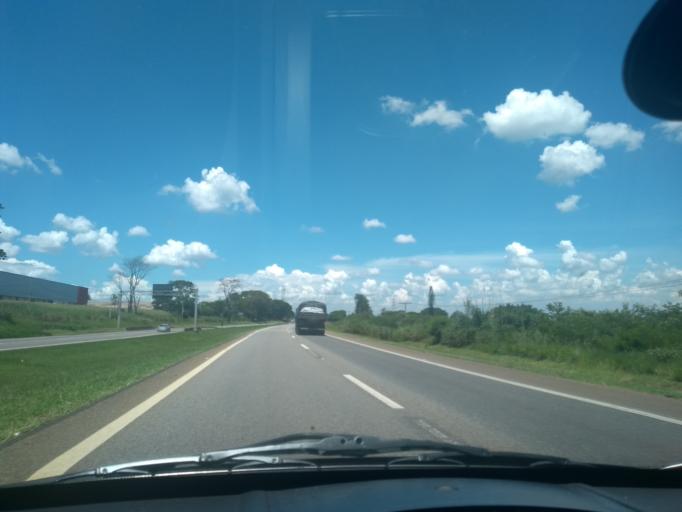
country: BR
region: Sao Paulo
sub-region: Mogi-Mirim
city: Mogi Mirim
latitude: -22.4861
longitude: -46.9812
